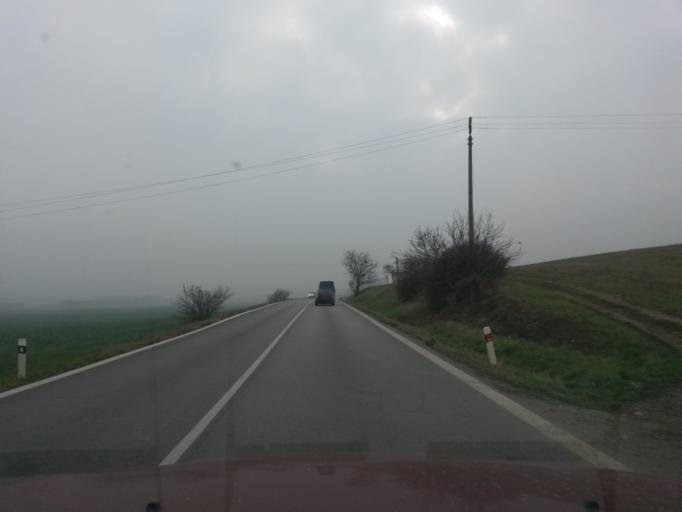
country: SK
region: Kosicky
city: Kosice
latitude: 48.8228
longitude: 21.2992
